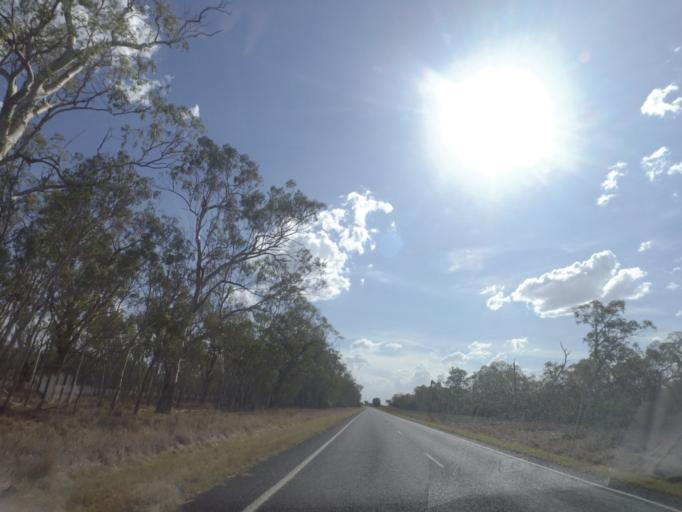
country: AU
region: New South Wales
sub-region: Moree Plains
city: Boggabilla
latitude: -28.5469
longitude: 150.8749
